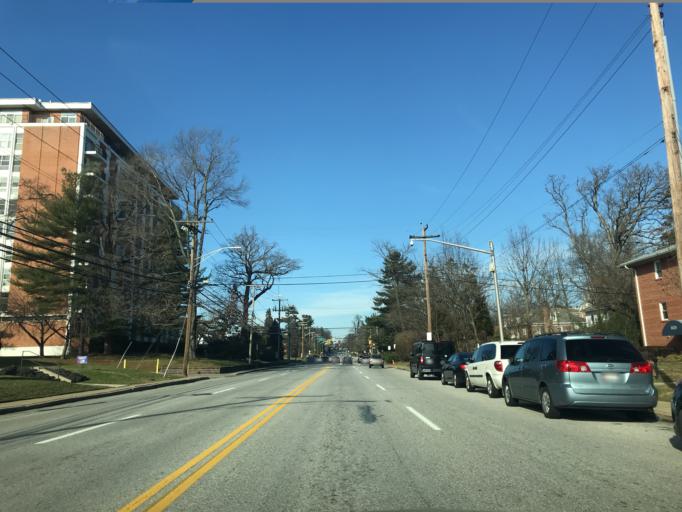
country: US
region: Maryland
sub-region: Baltimore County
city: Pikesville
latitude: 39.3614
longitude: -76.6986
